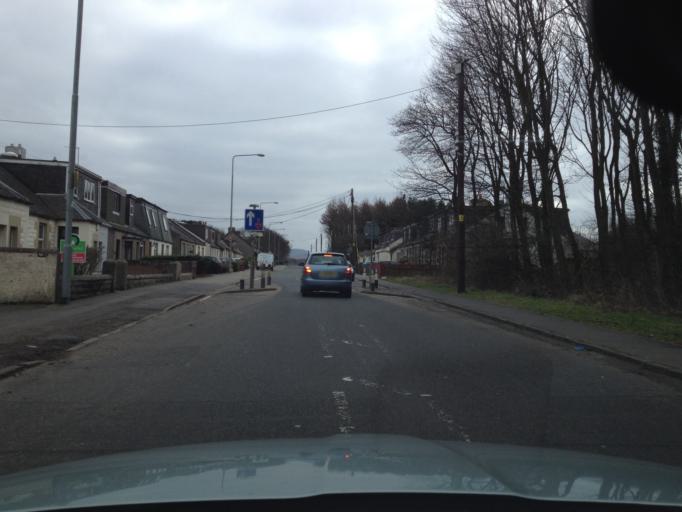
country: GB
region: Scotland
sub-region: West Lothian
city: Livingston
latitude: 55.9147
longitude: -3.5010
